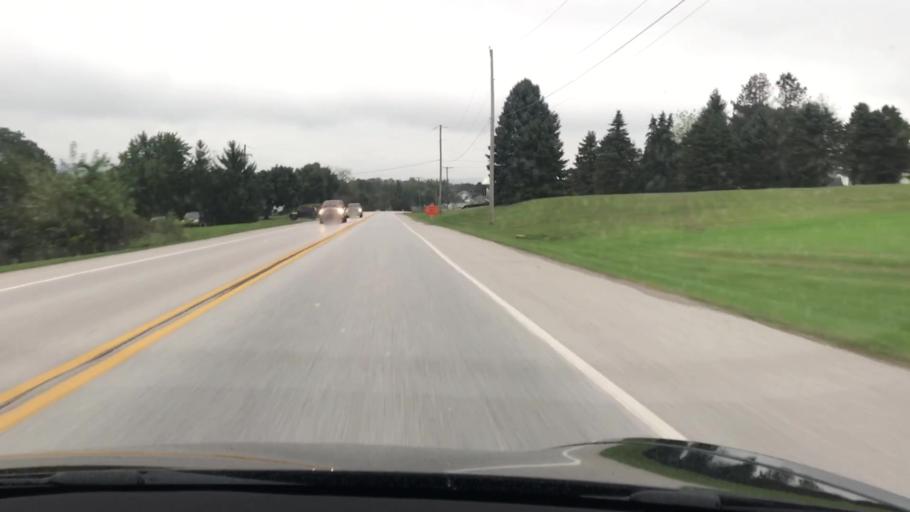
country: US
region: Pennsylvania
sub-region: York County
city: Dover
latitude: 39.9939
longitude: -76.8568
